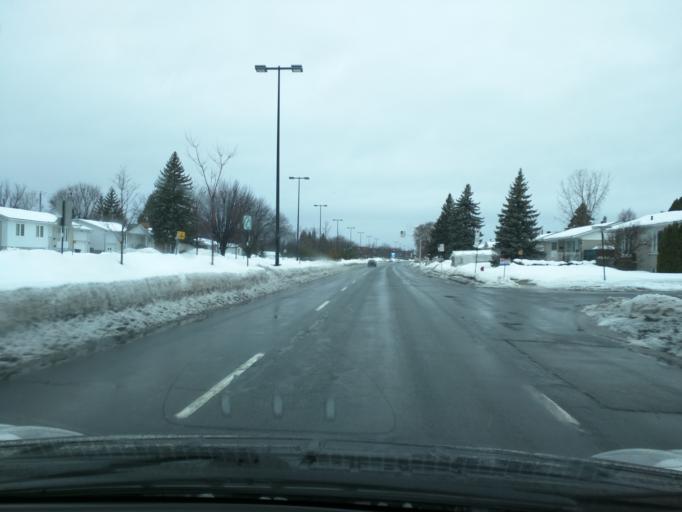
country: CA
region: Quebec
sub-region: Monteregie
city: Longueuil
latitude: 45.5308
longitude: -73.4580
